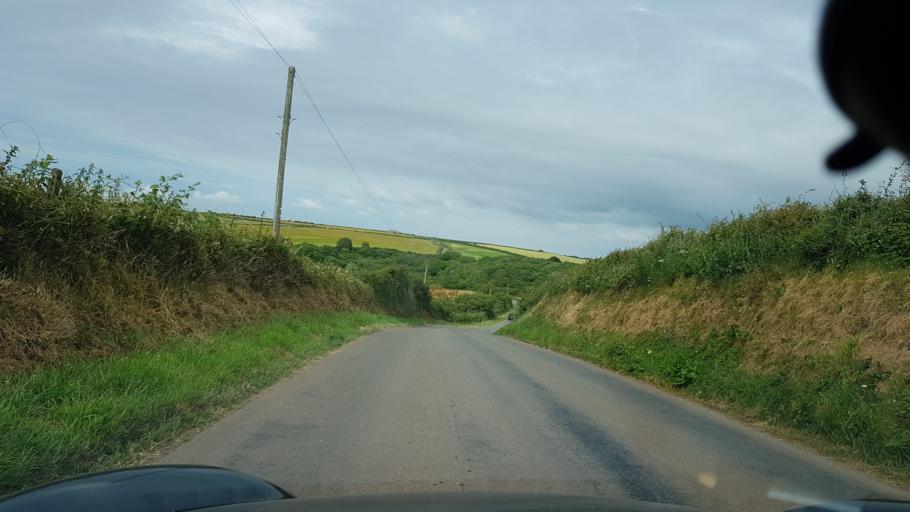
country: GB
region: Wales
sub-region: Pembrokeshire
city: Dale
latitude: 51.7348
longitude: -5.1607
